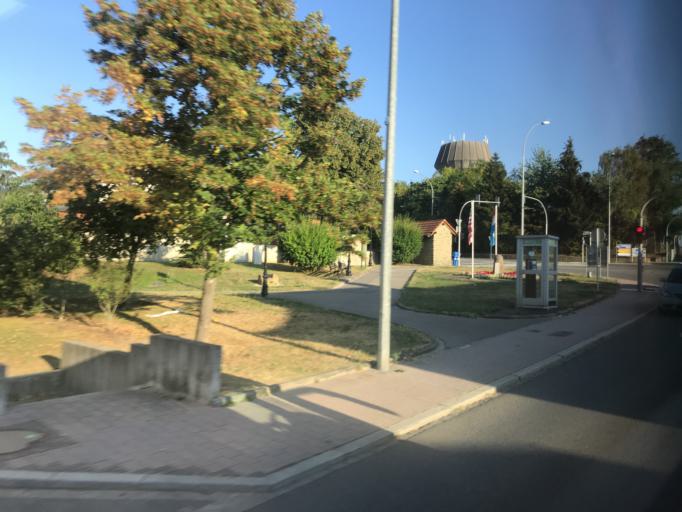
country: LU
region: Luxembourg
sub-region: Canton d'Esch-sur-Alzette
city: Frisange
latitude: 49.5164
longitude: 6.1877
